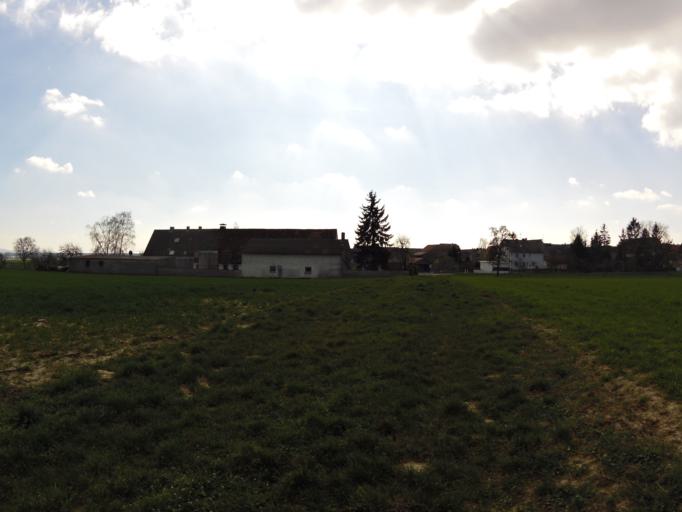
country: DE
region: Bavaria
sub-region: Regierungsbezirk Unterfranken
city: Biebelried
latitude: 49.7468
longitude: 10.0672
